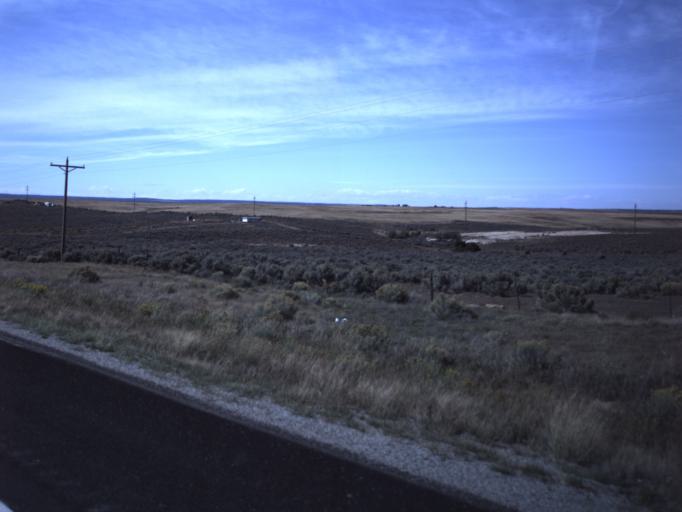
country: US
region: Utah
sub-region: San Juan County
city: Monticello
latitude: 37.8688
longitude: -109.2458
